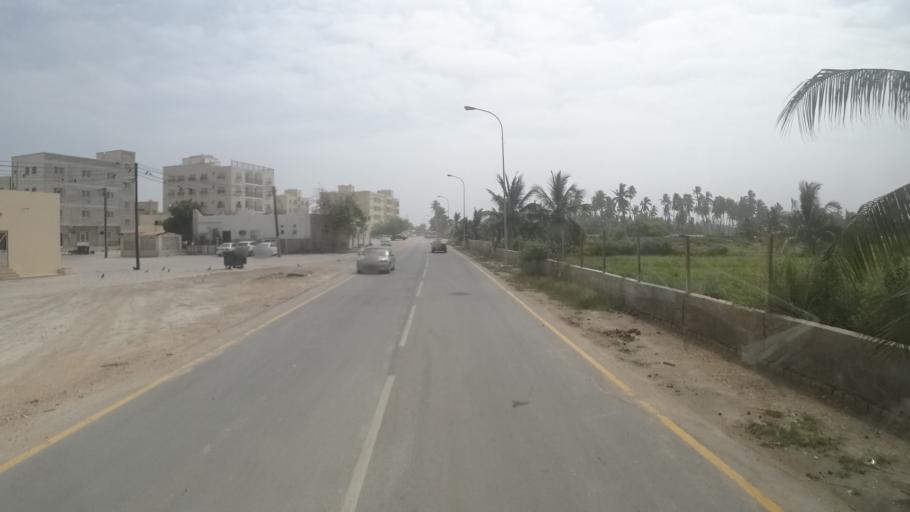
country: OM
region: Zufar
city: Salalah
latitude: 17.0123
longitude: 54.1619
